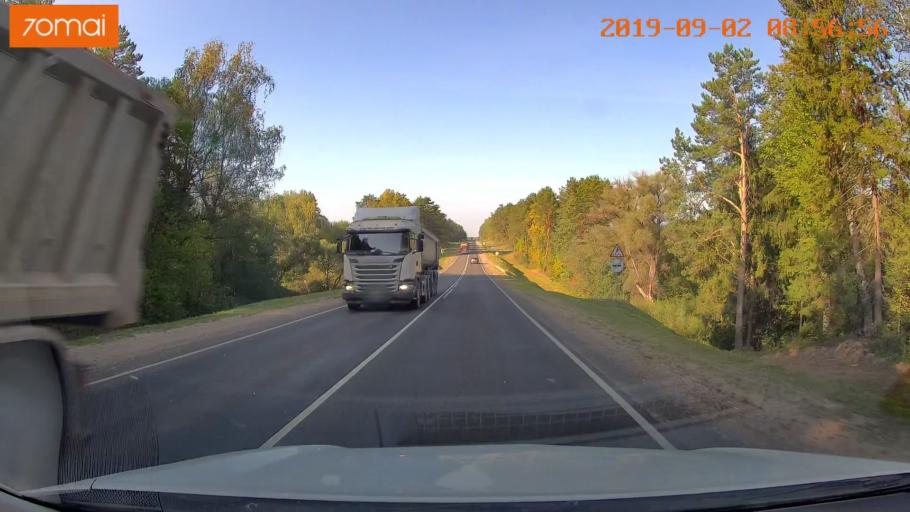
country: RU
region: Kaluga
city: Medyn'
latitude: 54.9411
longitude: 35.7804
